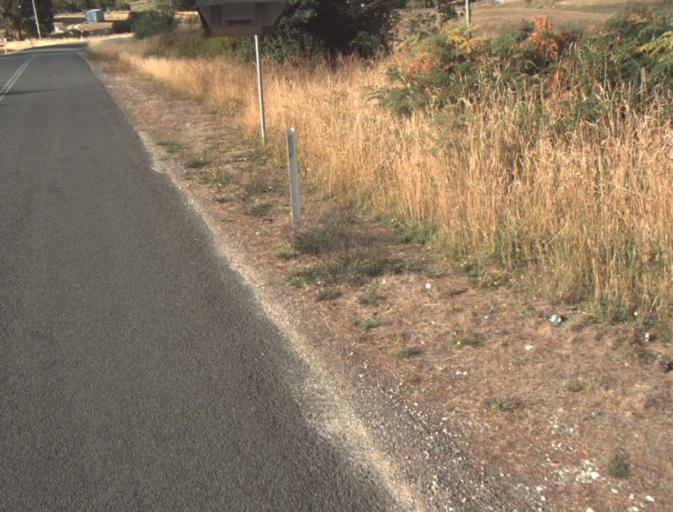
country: AU
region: Tasmania
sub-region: Launceston
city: Mayfield
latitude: -41.1737
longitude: 147.2300
